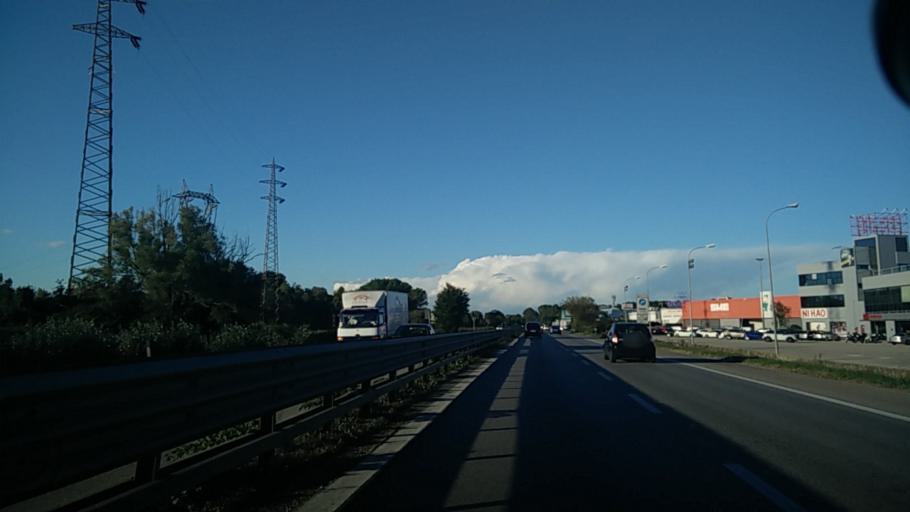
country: IT
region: Veneto
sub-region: Provincia di Venezia
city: Mestre
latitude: 45.4633
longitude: 12.2107
